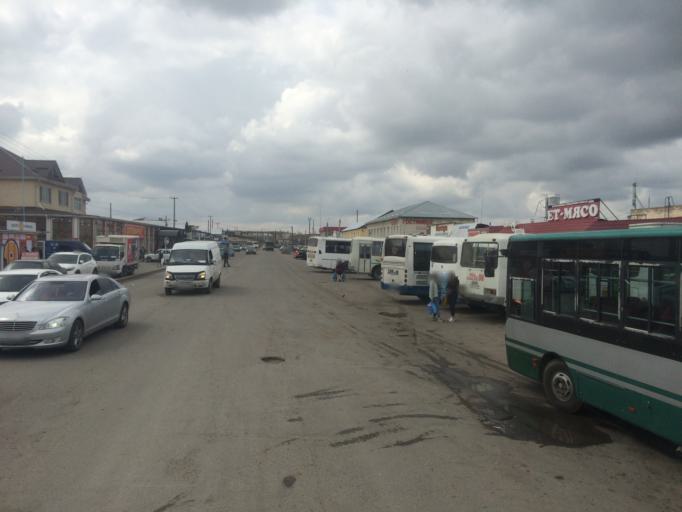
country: KZ
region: Zhambyl
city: Taraz
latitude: 42.9091
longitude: 71.4141
